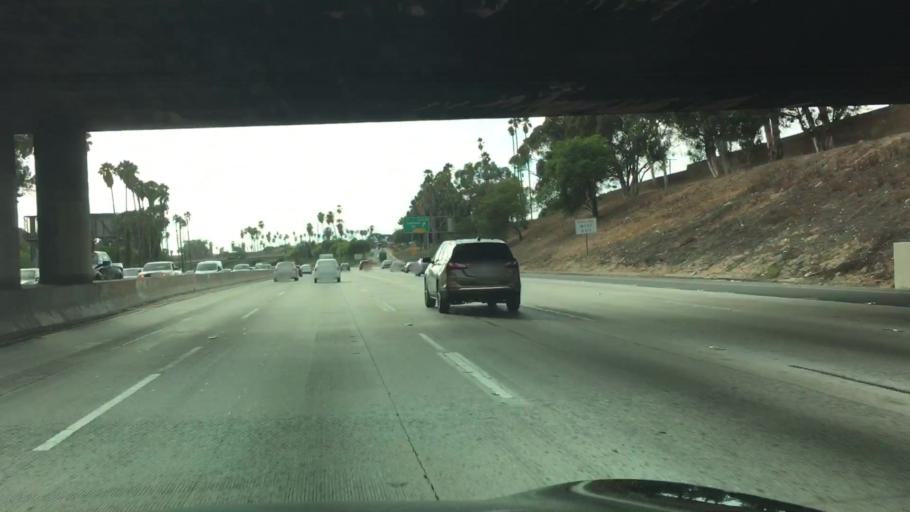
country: US
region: California
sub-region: Los Angeles County
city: Boyle Heights
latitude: 34.0337
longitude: -118.1881
